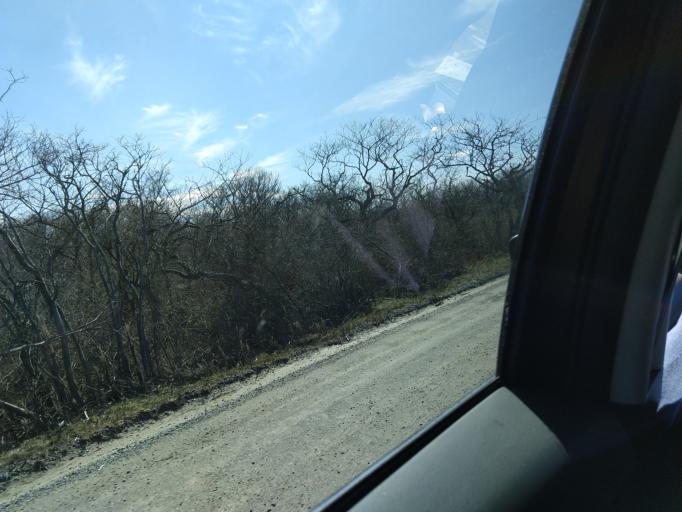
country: US
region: Massachusetts
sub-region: Essex County
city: Ipswich
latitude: 42.7210
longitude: -70.7825
